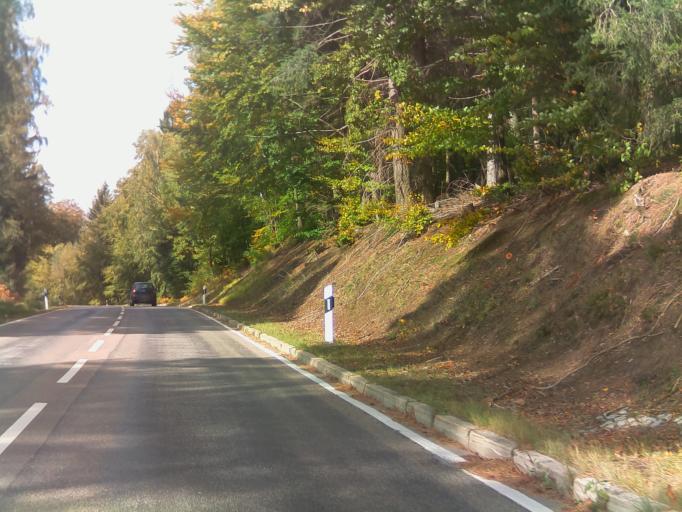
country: DE
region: Baden-Wuerttemberg
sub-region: Karlsruhe Region
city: Wilhelmsfeld
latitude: 49.4770
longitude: 8.7474
